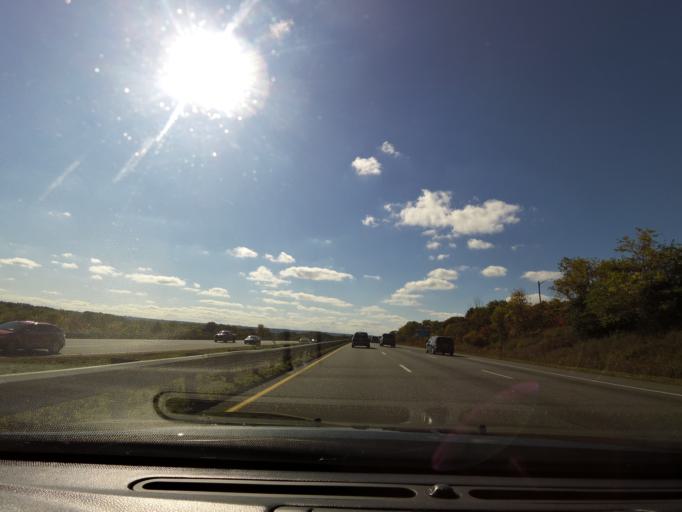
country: CA
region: Ontario
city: Hamilton
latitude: 43.3041
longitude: -79.8704
